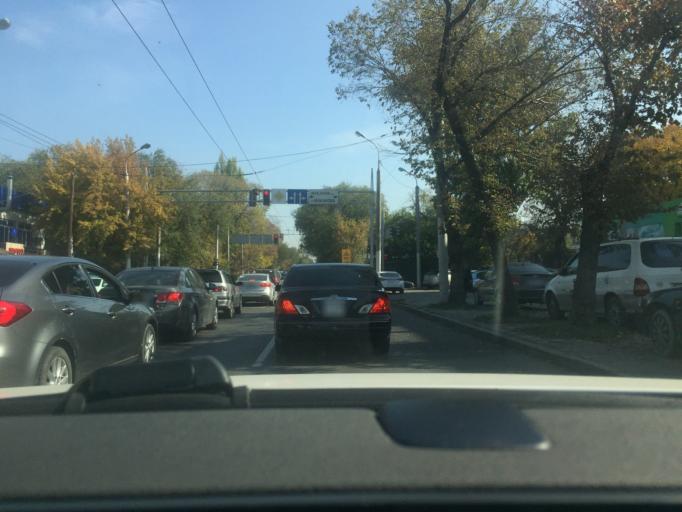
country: KZ
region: Almaty Qalasy
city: Almaty
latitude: 43.2577
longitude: 76.9135
